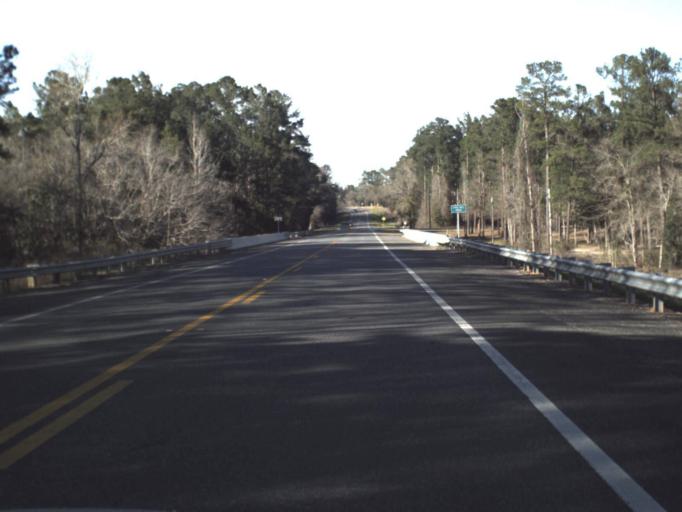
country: US
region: Florida
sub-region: Calhoun County
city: Blountstown
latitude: 30.4441
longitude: -85.1829
